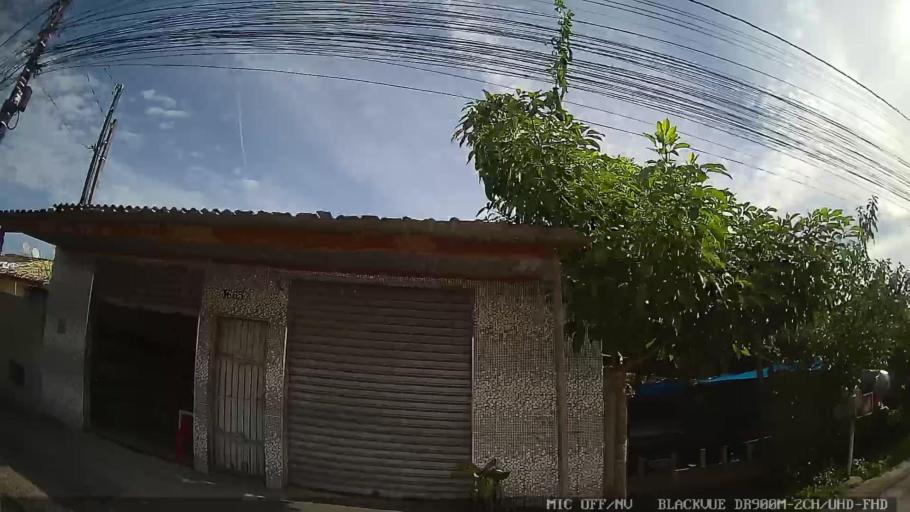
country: BR
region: Sao Paulo
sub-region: Itanhaem
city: Itanhaem
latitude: -24.1560
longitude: -46.7736
